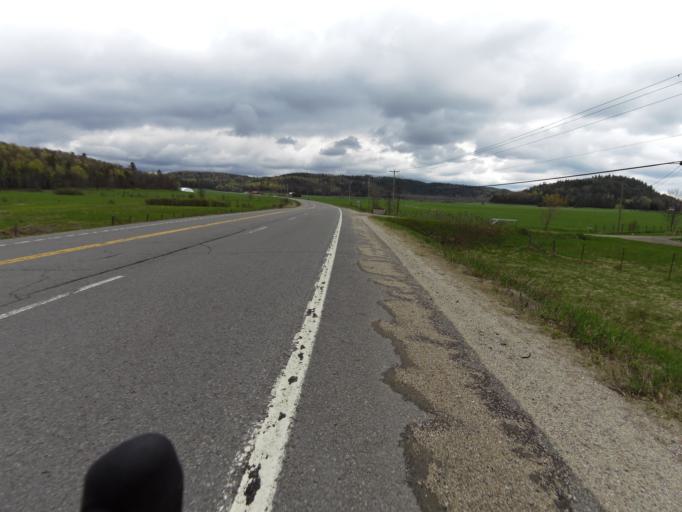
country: CA
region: Quebec
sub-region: Outaouais
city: Wakefield
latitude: 45.6437
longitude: -75.9027
